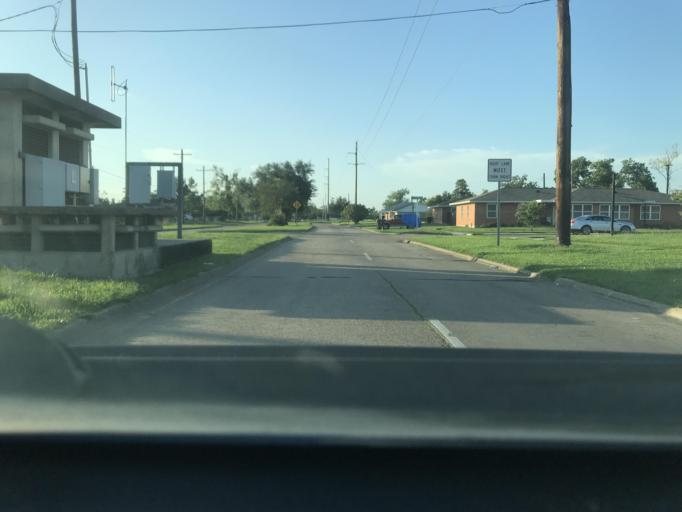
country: US
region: Louisiana
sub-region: Calcasieu Parish
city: Lake Charles
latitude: 30.2553
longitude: -93.1952
